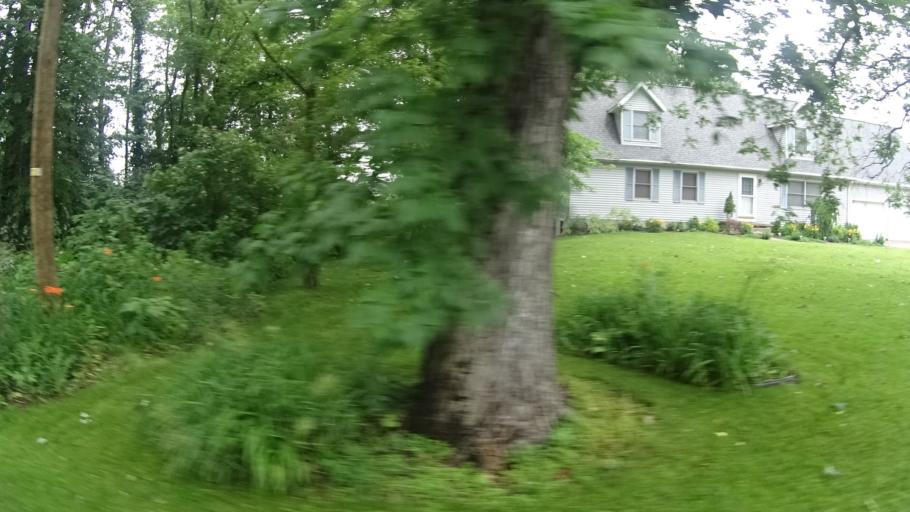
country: US
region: Ohio
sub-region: Erie County
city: Huron
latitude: 41.3548
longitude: -82.5498
